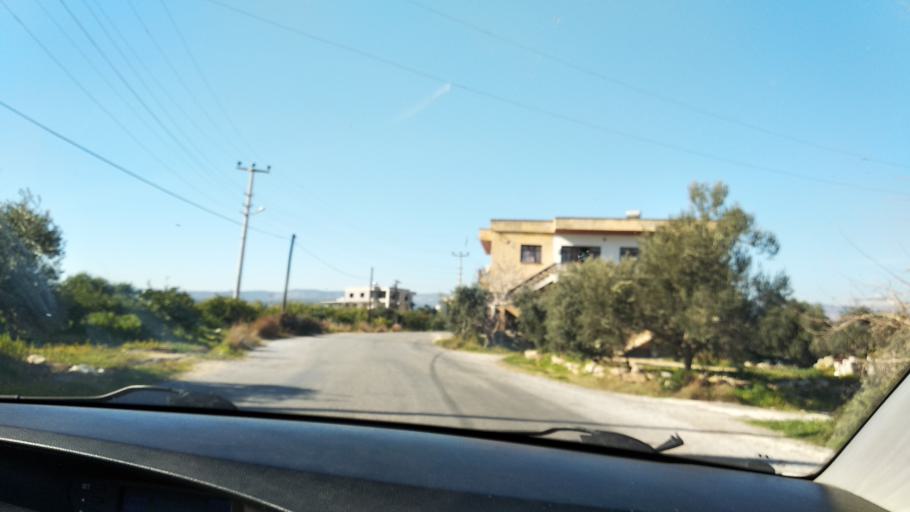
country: TR
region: Mersin
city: Tomuk
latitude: 36.6647
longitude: 34.3611
